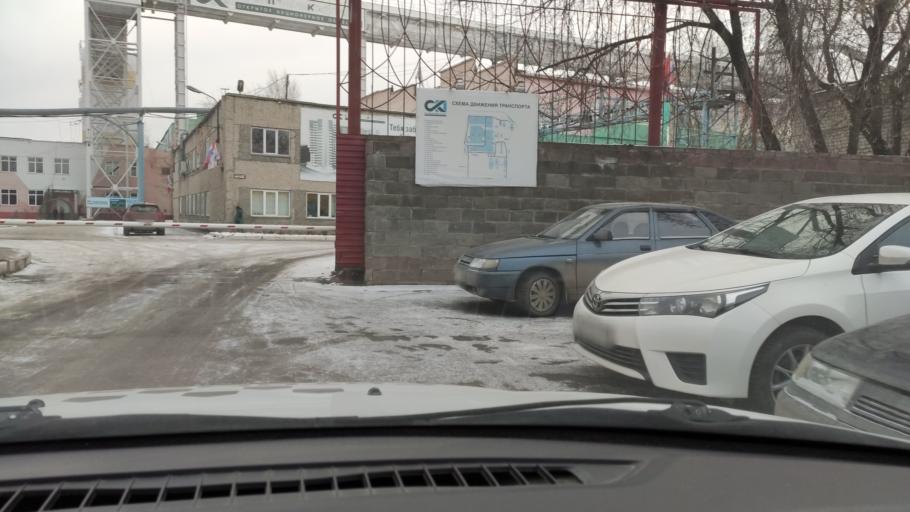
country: RU
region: Perm
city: Perm
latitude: 57.9835
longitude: 56.2639
